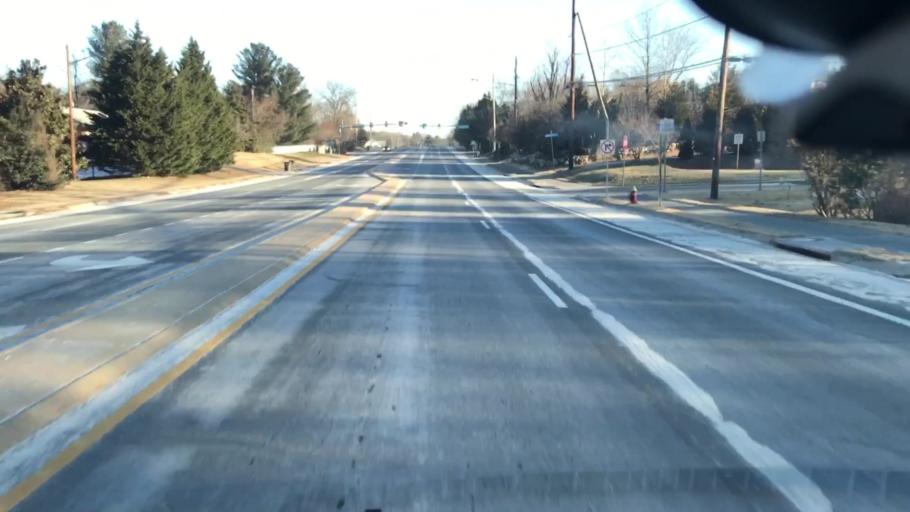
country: US
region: Virginia
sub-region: Fairfax County
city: Newington
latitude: 38.7522
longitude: -77.1658
